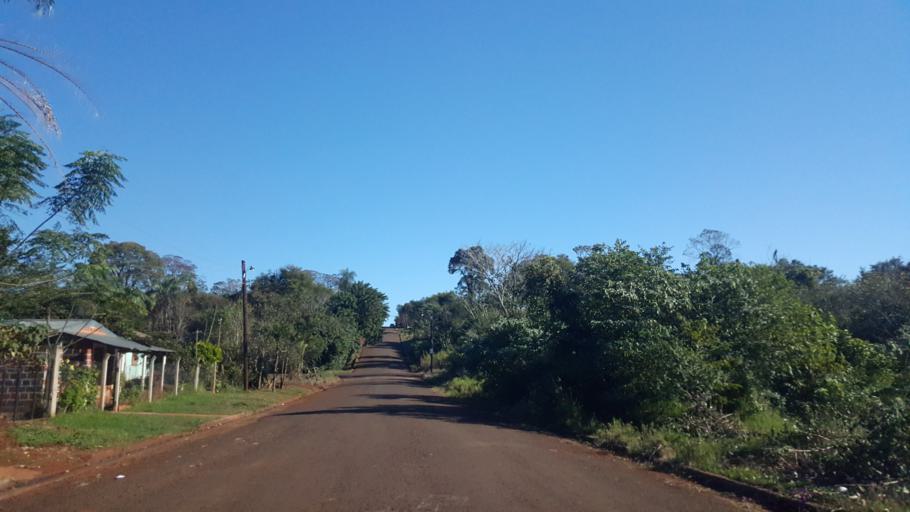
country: AR
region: Misiones
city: Gobernador Roca
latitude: -27.1881
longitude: -55.4679
